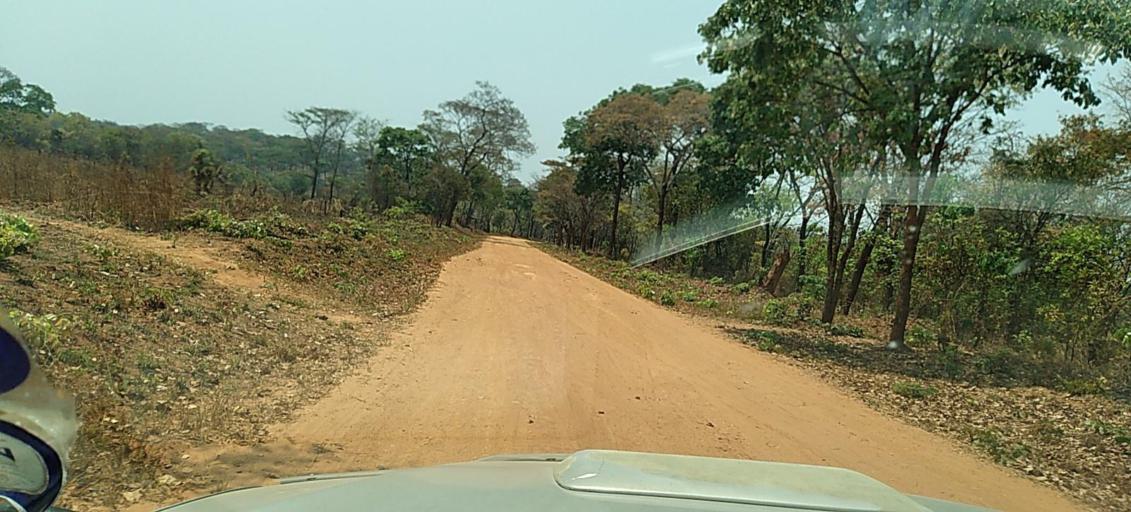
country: ZM
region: North-Western
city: Kasempa
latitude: -13.5455
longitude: 26.0393
